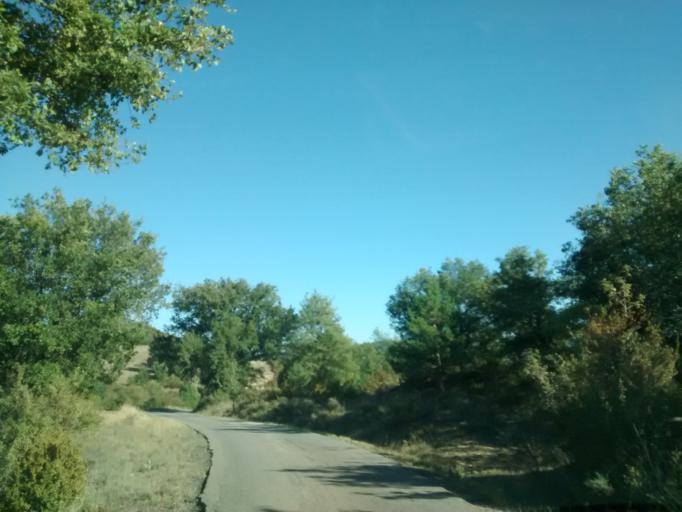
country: ES
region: Aragon
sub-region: Provincia de Huesca
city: Santa Cruz de la Seros
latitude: 42.4391
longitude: -0.6647
